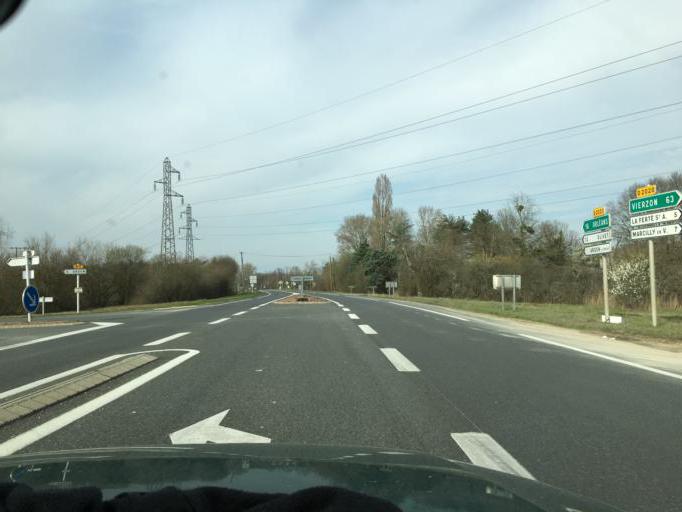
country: FR
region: Centre
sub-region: Departement du Loiret
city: La Ferte-Saint-Aubin
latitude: 47.7708
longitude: 1.9371
